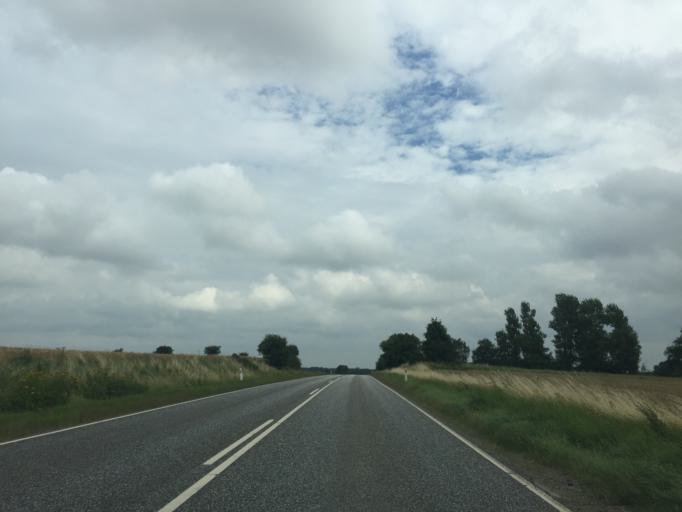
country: DK
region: Central Jutland
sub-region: Randers Kommune
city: Langa
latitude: 56.3851
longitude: 9.9612
